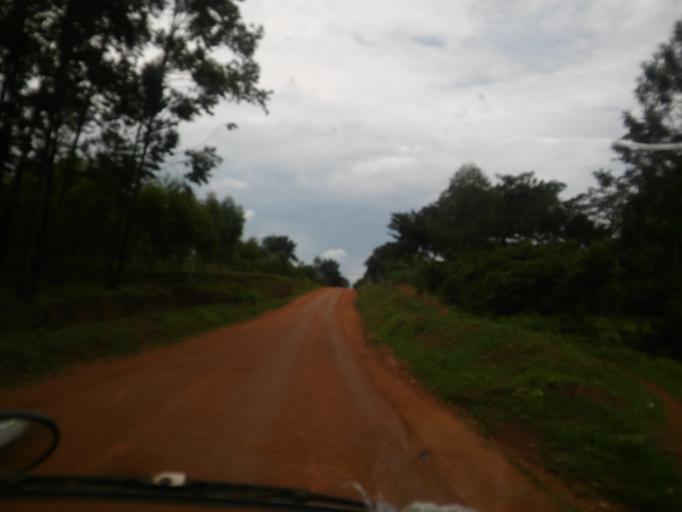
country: UG
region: Eastern Region
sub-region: Bududa District
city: Bududa
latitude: 0.9485
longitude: 34.2450
